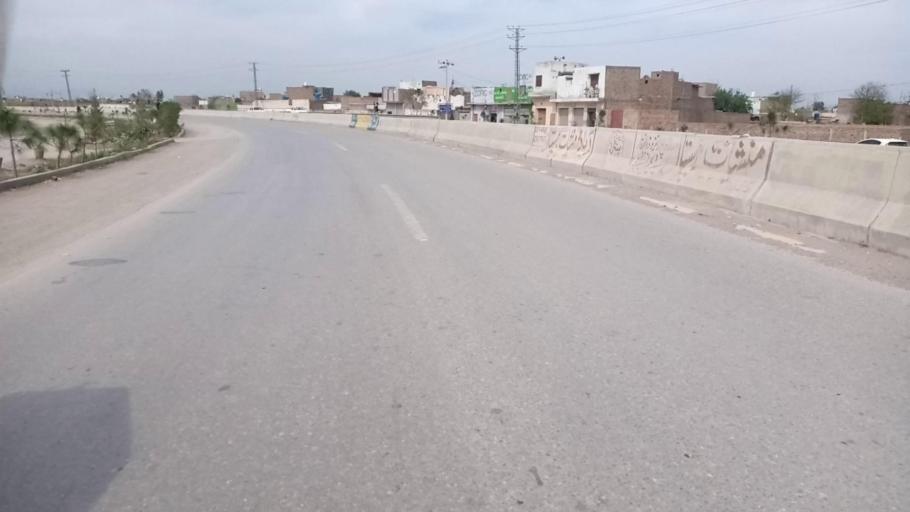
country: PK
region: Khyber Pakhtunkhwa
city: Peshawar
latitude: 34.0333
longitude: 71.6422
